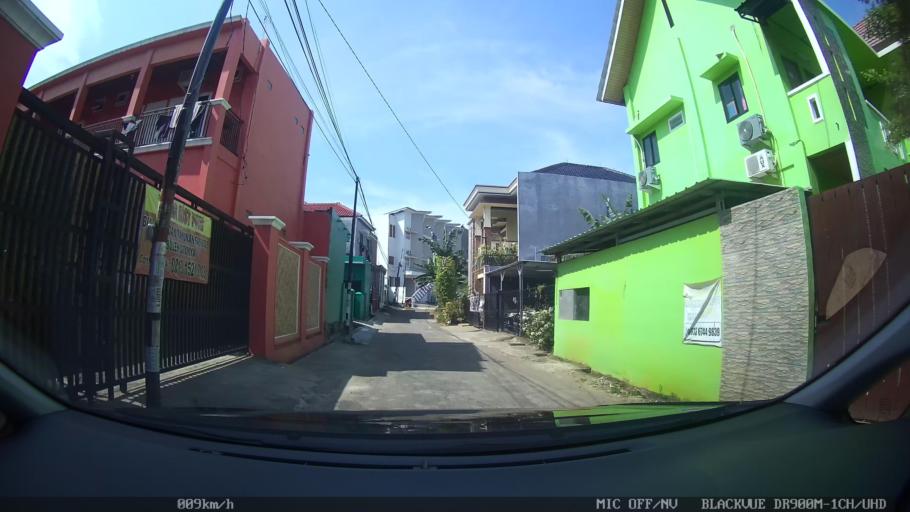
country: ID
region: Lampung
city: Kedaton
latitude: -5.3711
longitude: 105.2438
